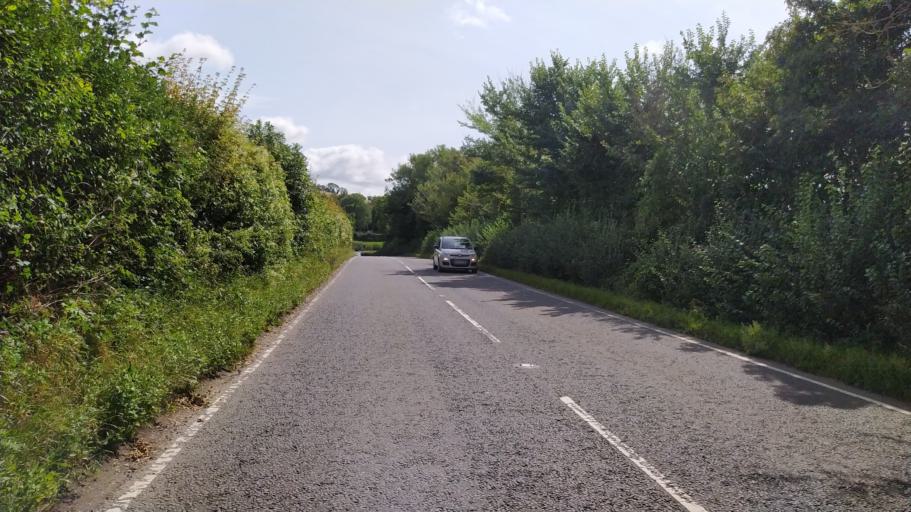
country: GB
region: England
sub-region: Dorset
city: Blandford Forum
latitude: 50.8950
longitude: -2.1936
